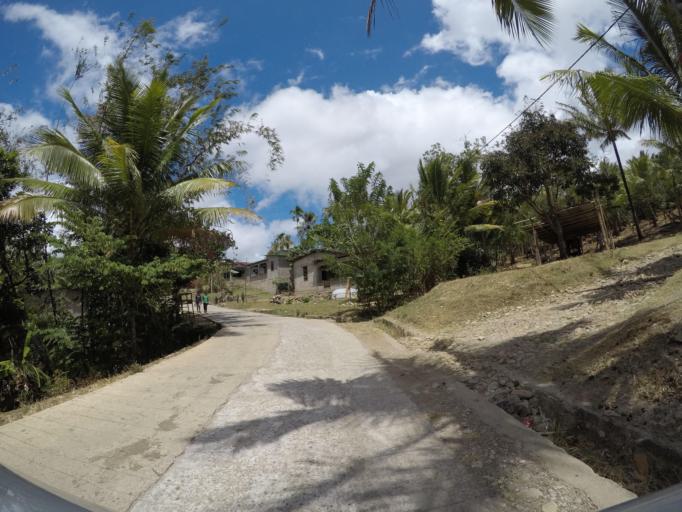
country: TL
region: Lautem
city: Lospalos
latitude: -8.5458
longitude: 126.8327
